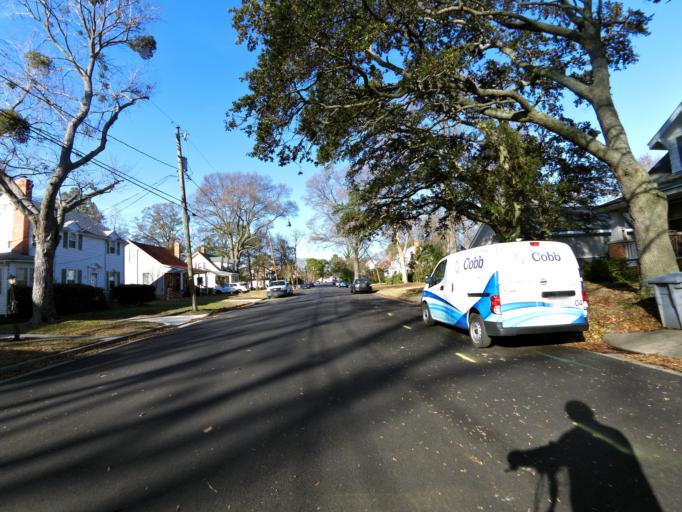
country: US
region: Virginia
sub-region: City of Hampton
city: Hampton
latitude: 37.0043
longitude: -76.3709
